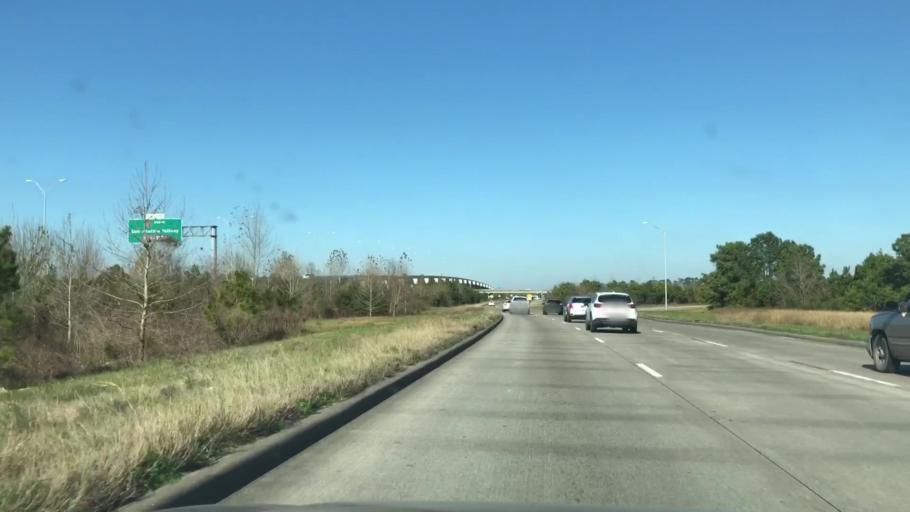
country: US
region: Texas
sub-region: Harris County
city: Cloverleaf
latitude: 29.8287
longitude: -95.1712
